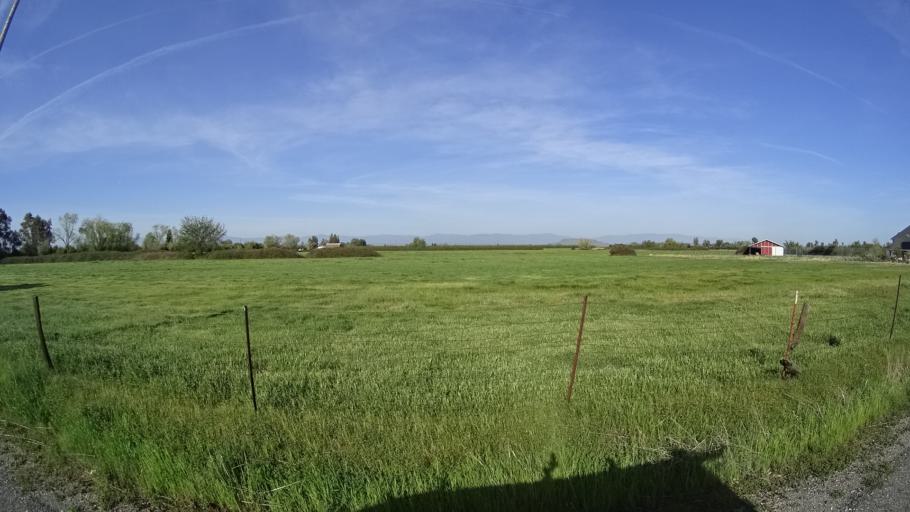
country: US
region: California
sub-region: Glenn County
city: Orland
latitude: 39.7202
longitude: -122.2157
